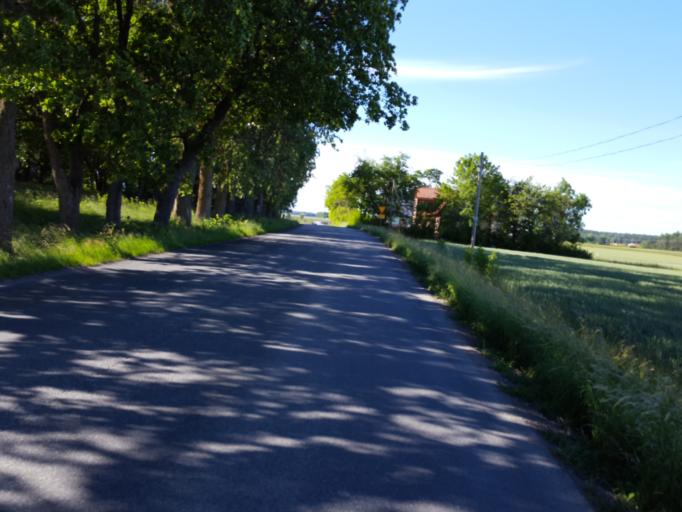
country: SE
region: Uppsala
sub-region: Uppsala Kommun
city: Saevja
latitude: 59.8423
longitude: 17.7415
